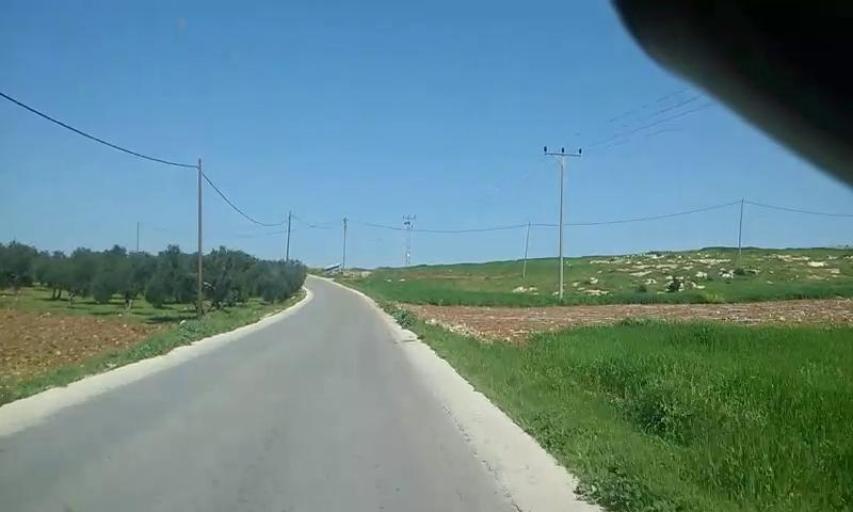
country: PS
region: West Bank
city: Al Majd
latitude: 31.4730
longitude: 34.9487
